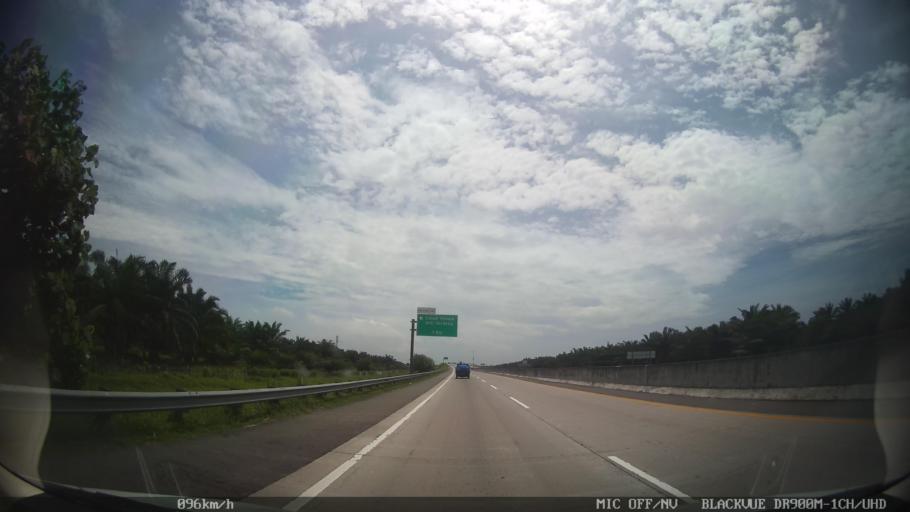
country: ID
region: North Sumatra
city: Perbaungan
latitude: 3.5316
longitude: 98.8803
